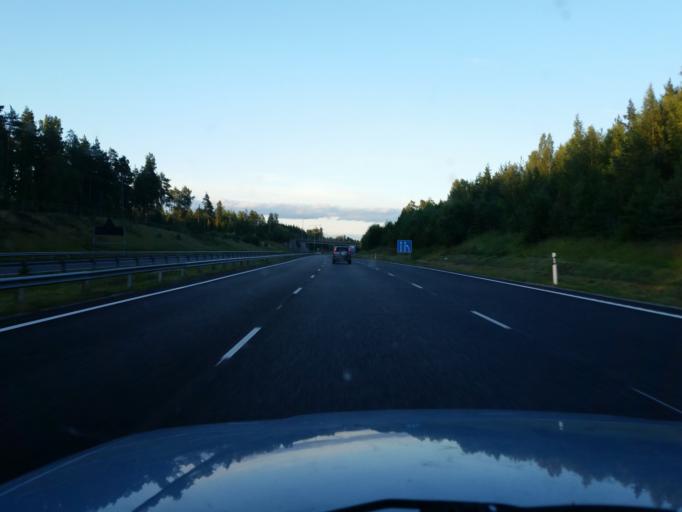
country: FI
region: Varsinais-Suomi
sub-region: Turku
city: Paimio
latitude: 60.4249
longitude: 22.7044
